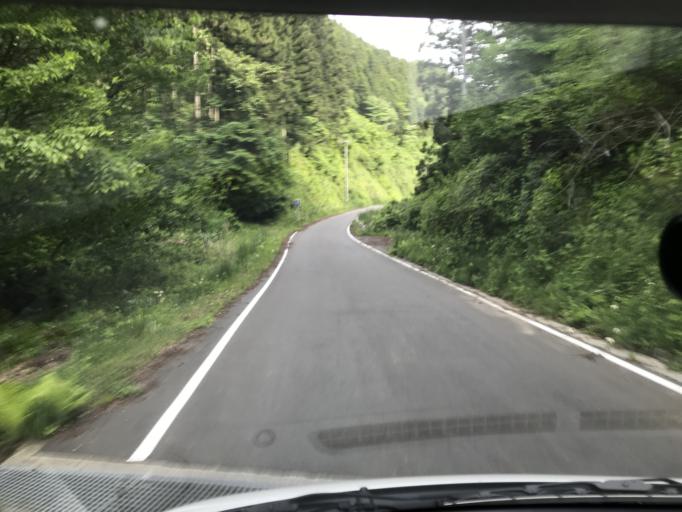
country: JP
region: Miyagi
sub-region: Oshika Gun
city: Onagawa Cho
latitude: 38.6783
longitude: 141.3475
